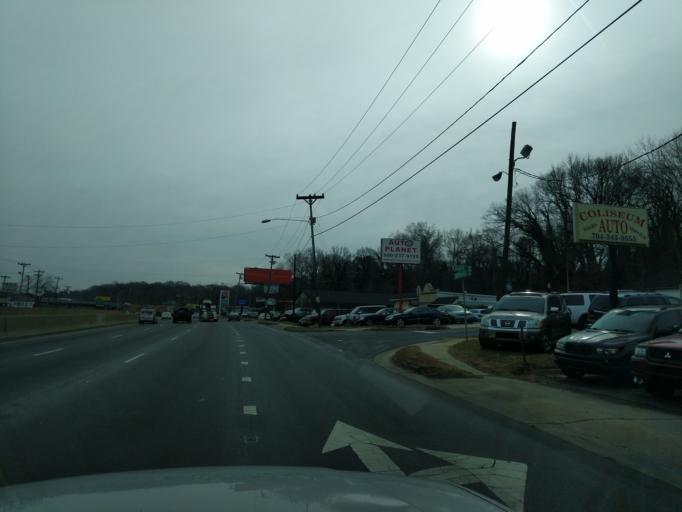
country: US
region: North Carolina
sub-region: Mecklenburg County
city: Charlotte
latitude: 35.2036
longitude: -80.7922
